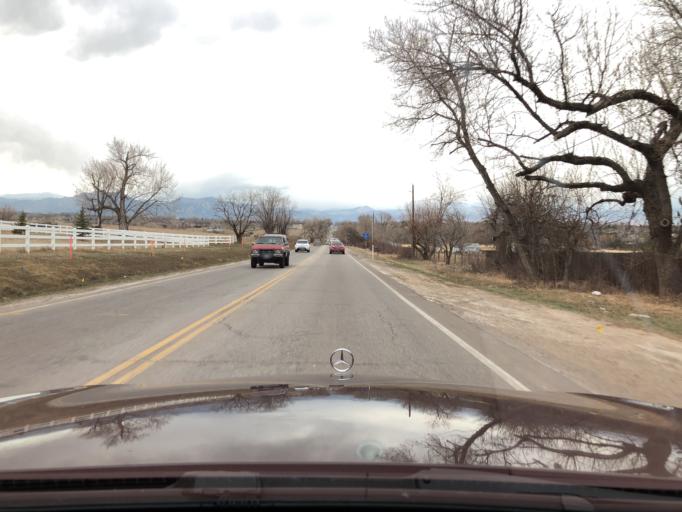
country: US
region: Colorado
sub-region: Boulder County
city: Lafayette
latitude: 40.0147
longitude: -105.1122
